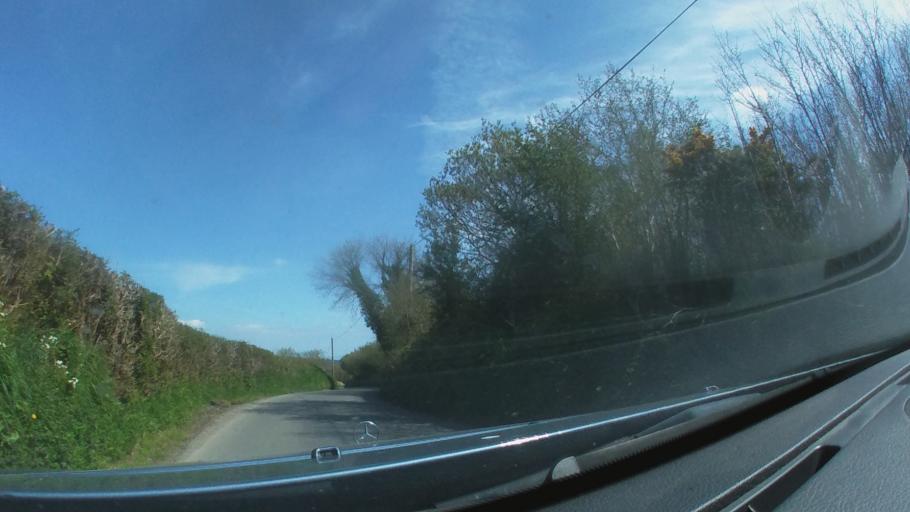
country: IE
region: Leinster
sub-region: Kilkenny
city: Callan
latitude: 52.6261
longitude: -7.4532
